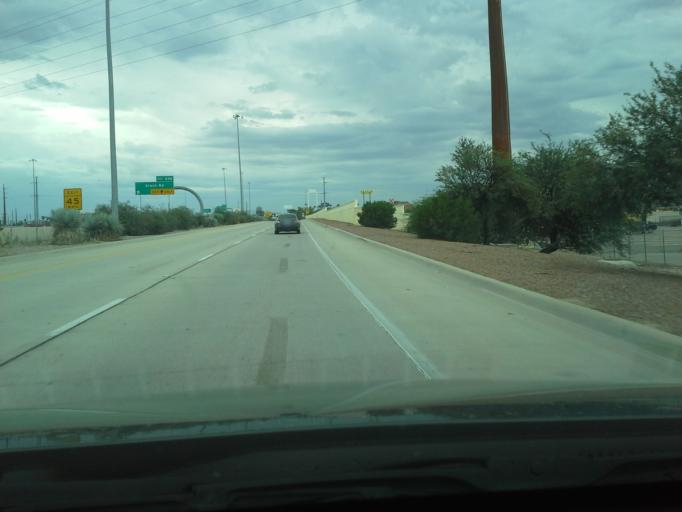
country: US
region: Arizona
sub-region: Pima County
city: Flowing Wells
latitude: 32.2548
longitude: -110.9969
